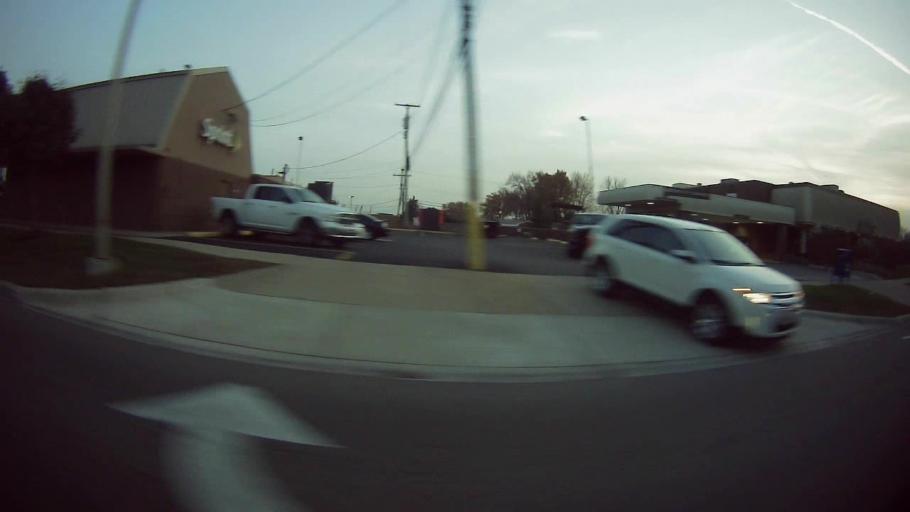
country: US
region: Michigan
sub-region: Oakland County
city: Madison Heights
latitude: 42.5052
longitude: -83.0835
